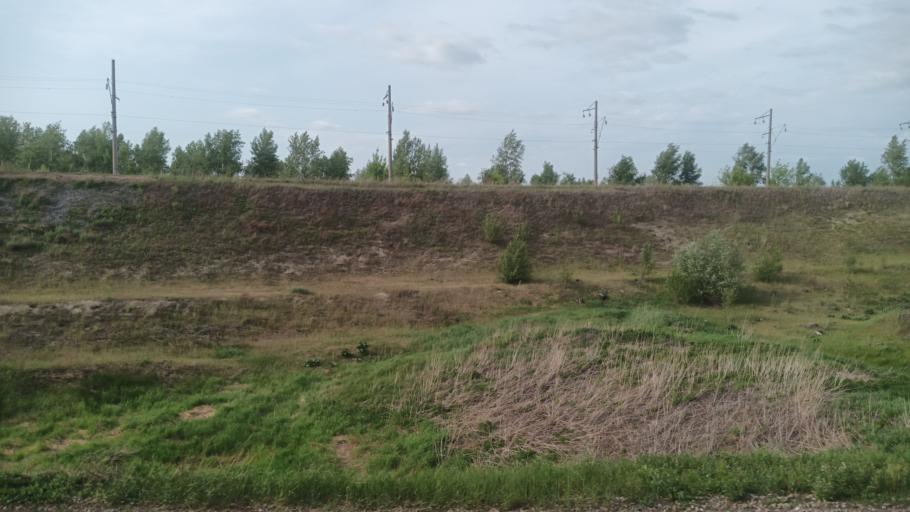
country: RU
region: Altai Krai
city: Zaton
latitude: 53.3681
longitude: 83.8496
